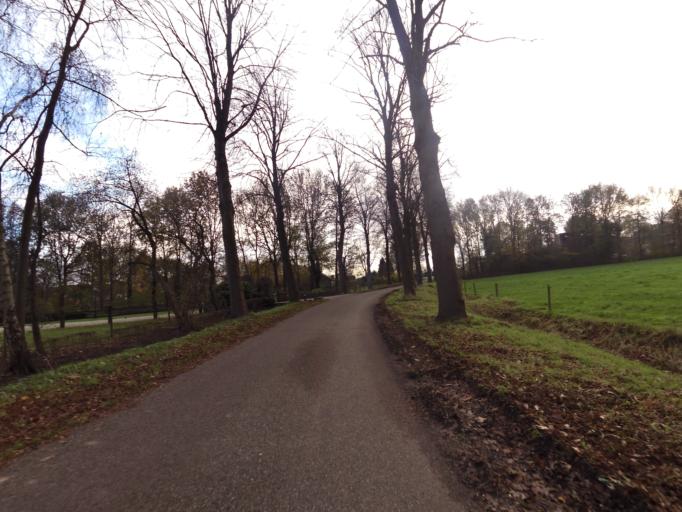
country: NL
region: Gelderland
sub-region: Gemeente Montferland
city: s-Heerenberg
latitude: 51.9005
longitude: 6.2686
